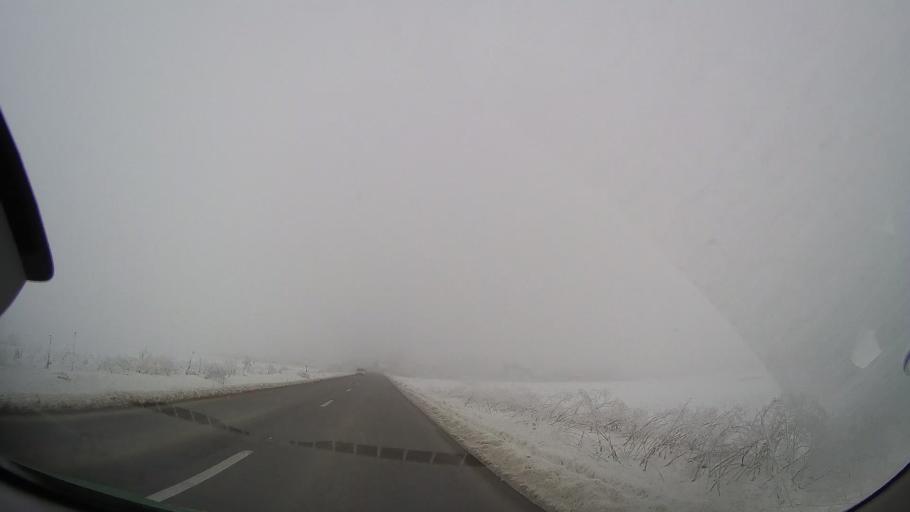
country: RO
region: Iasi
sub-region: Comuna Mogosesti-Siret
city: Mogosesti-Siret
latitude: 47.1557
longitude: 26.7766
